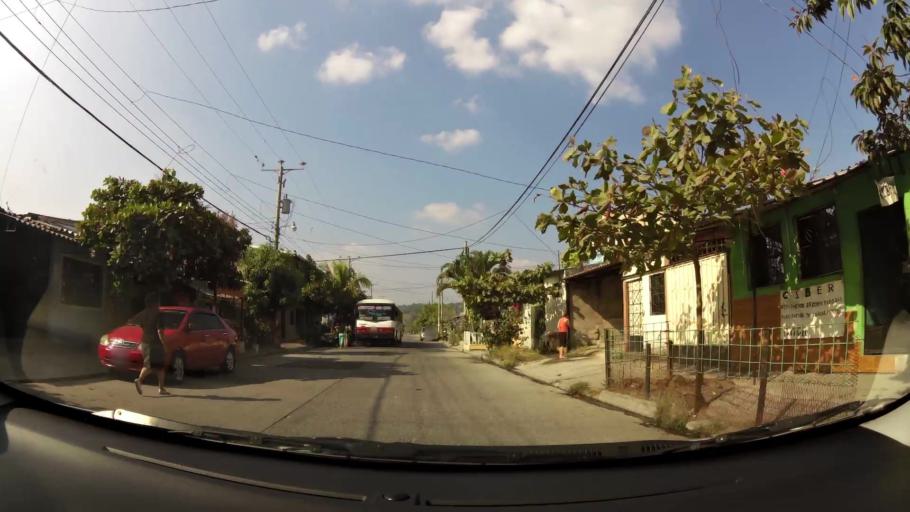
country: SV
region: San Salvador
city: Ilopango
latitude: 13.7268
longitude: -89.1093
